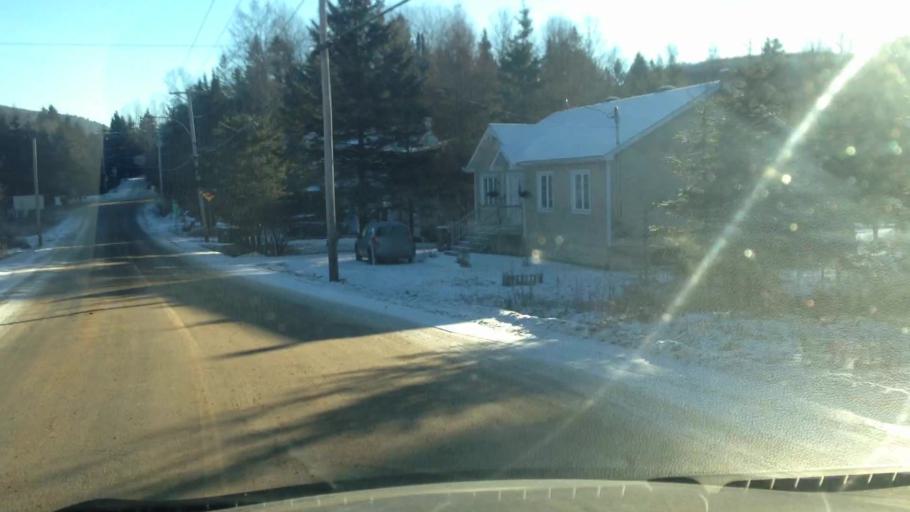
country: CA
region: Quebec
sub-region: Laurentides
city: Mont-Tremblant
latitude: 45.9404
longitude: -74.5472
